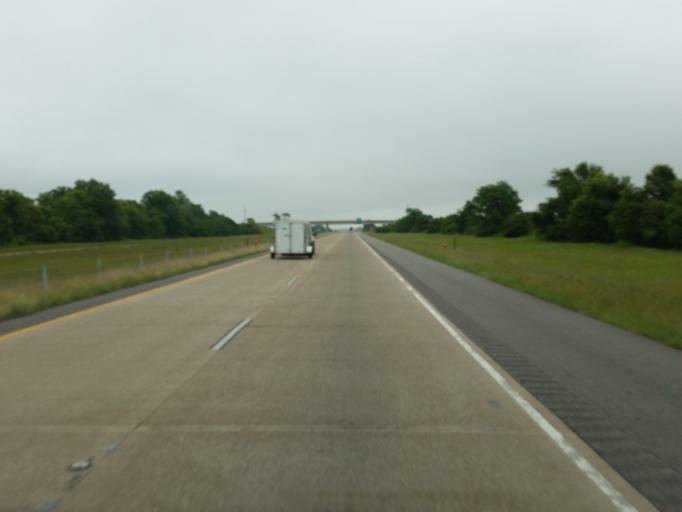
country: US
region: Mississippi
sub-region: Warren County
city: Vicksburg
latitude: 32.3305
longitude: -91.0290
